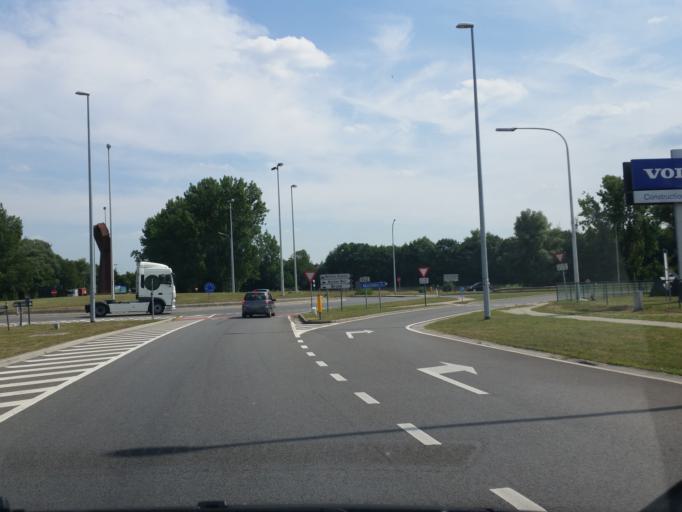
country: BE
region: Flanders
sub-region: Provincie Vlaams-Brabant
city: Machelen
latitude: 50.9223
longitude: 4.4430
